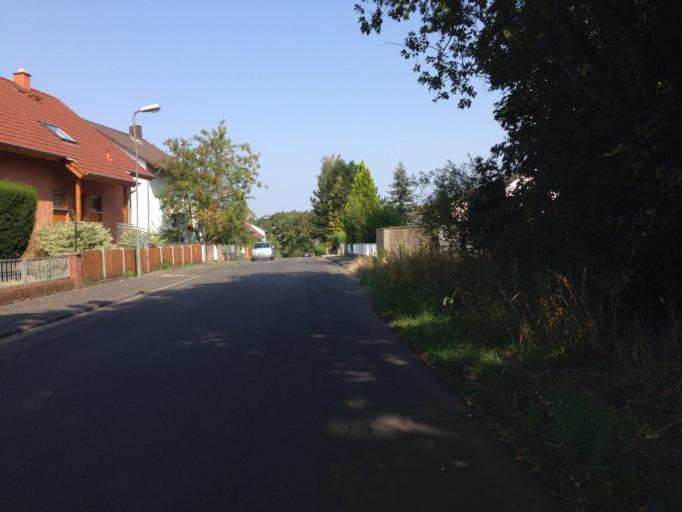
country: DE
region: Hesse
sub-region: Regierungsbezirk Giessen
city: Giessen
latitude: 50.5922
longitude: 8.7077
